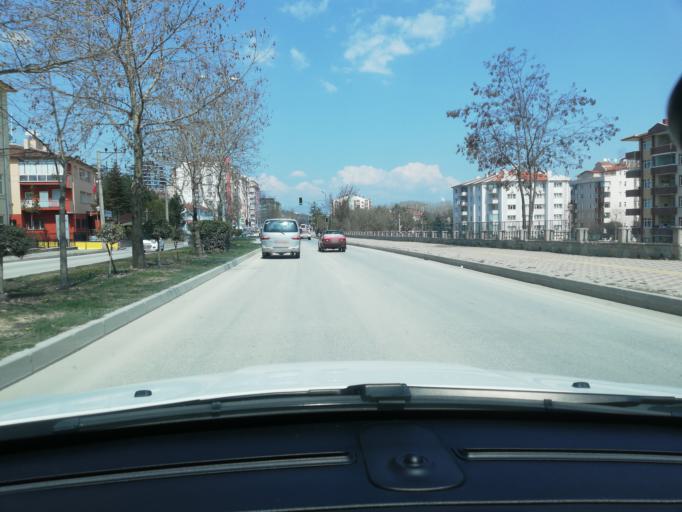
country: TR
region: Kastamonu
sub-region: Cide
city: Kastamonu
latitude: 41.4025
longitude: 33.7830
